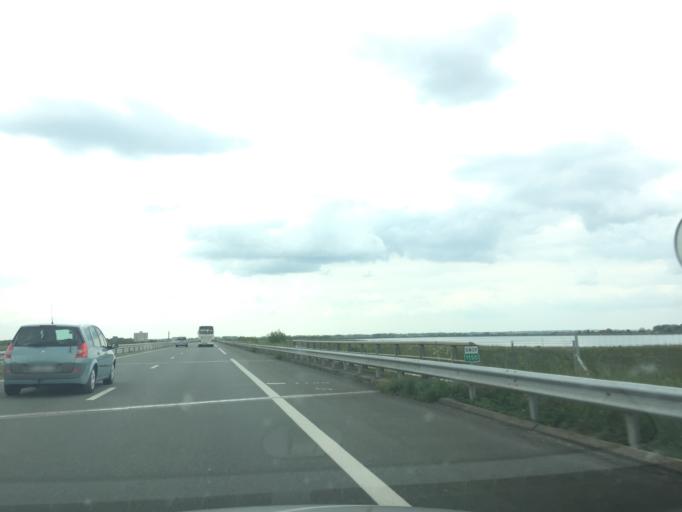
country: FR
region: Pays de la Loire
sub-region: Departement de la Vendee
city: Benet
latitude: 46.3953
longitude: -0.6399
